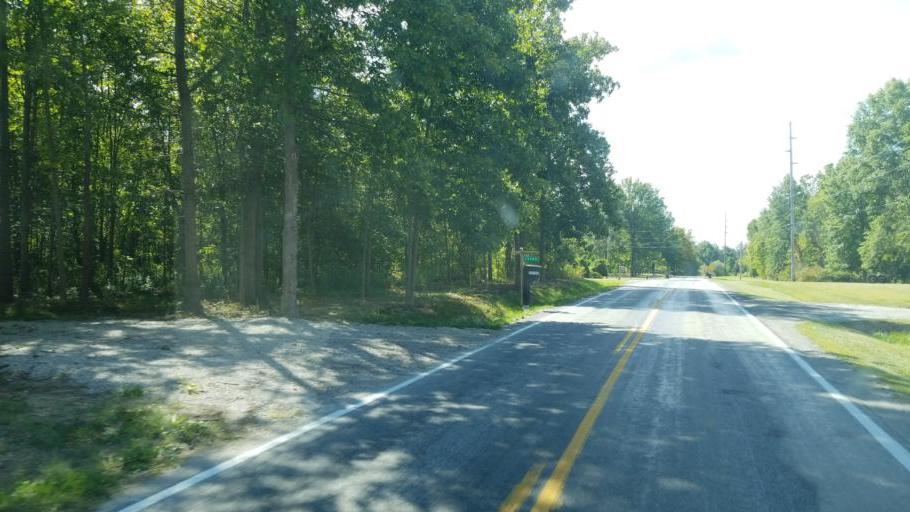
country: US
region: Ohio
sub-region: Lorain County
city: Lagrange
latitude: 41.1790
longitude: -82.1087
